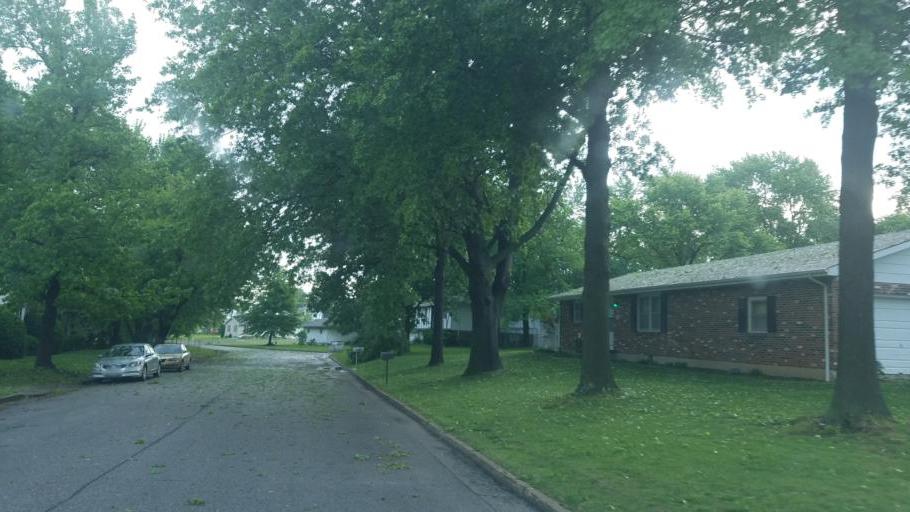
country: US
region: Missouri
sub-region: Moniteau County
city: California
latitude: 38.6254
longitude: -92.5744
